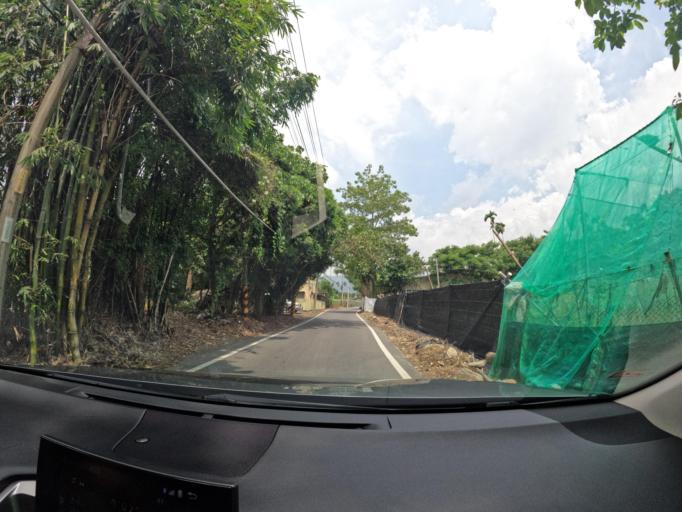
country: TW
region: Taiwan
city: Lugu
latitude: 23.8101
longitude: 120.8223
